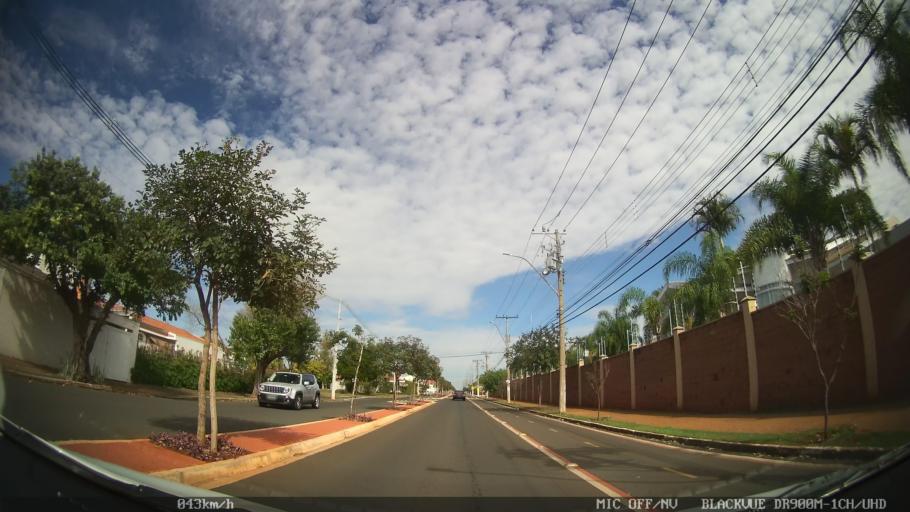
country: BR
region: Sao Paulo
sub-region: Santa Barbara D'Oeste
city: Santa Barbara d'Oeste
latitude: -22.7588
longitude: -47.4275
